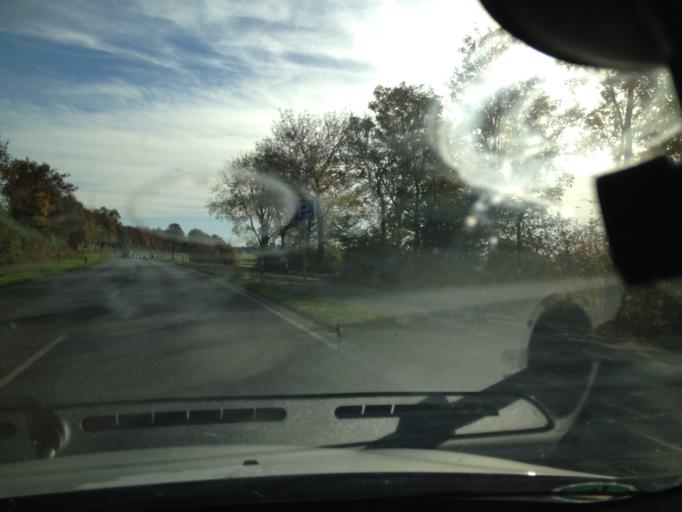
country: DE
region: Bavaria
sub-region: Swabia
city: Bobingen
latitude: 48.2987
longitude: 10.8511
